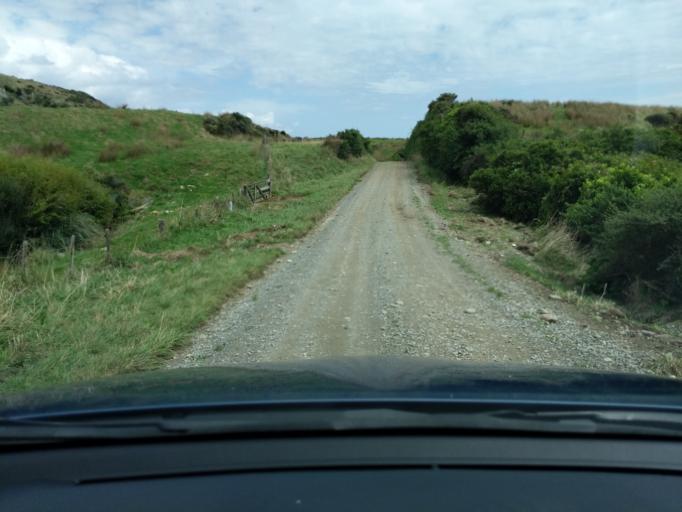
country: NZ
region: Tasman
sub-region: Tasman District
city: Takaka
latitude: -40.6665
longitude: 172.4066
